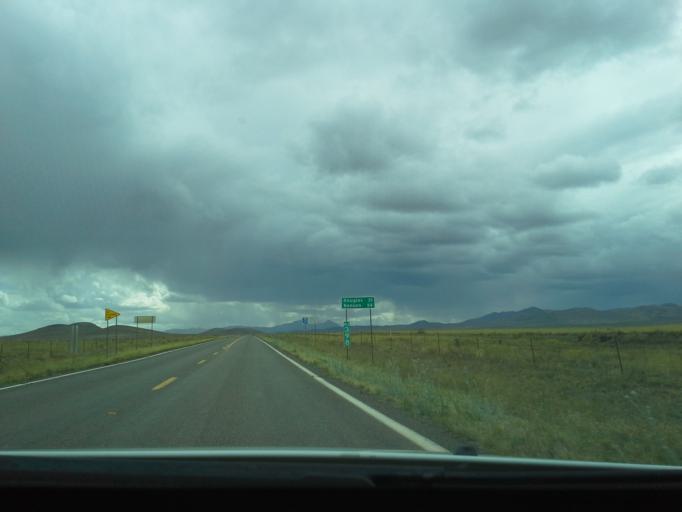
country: US
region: Arizona
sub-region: Cochise County
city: Douglas
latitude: 31.6115
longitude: -109.2200
